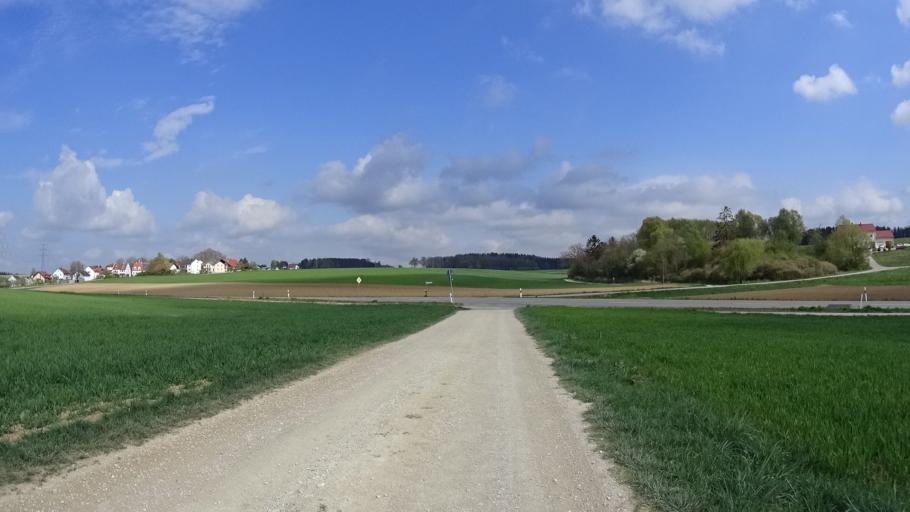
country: DE
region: Bavaria
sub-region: Upper Bavaria
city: Wettstetten
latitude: 48.8398
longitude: 11.4010
